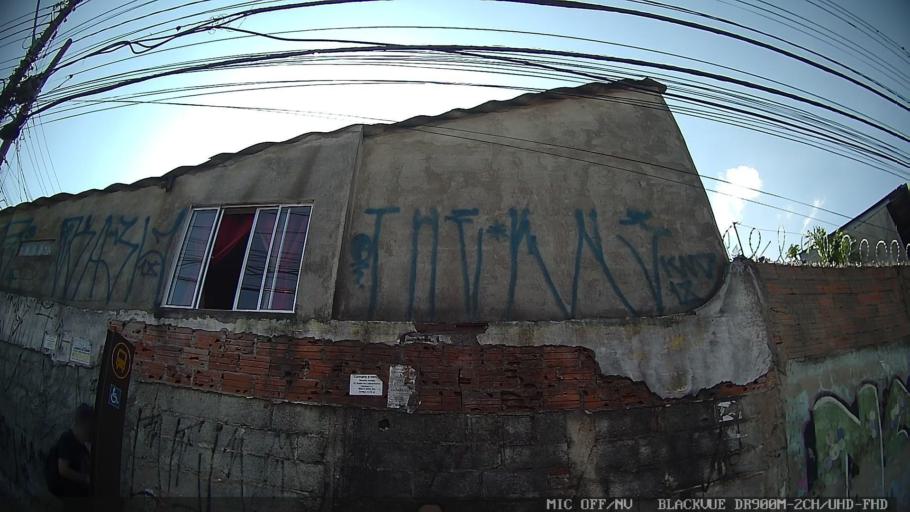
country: BR
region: Sao Paulo
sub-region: Ferraz De Vasconcelos
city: Ferraz de Vasconcelos
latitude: -23.5252
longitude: -46.4318
